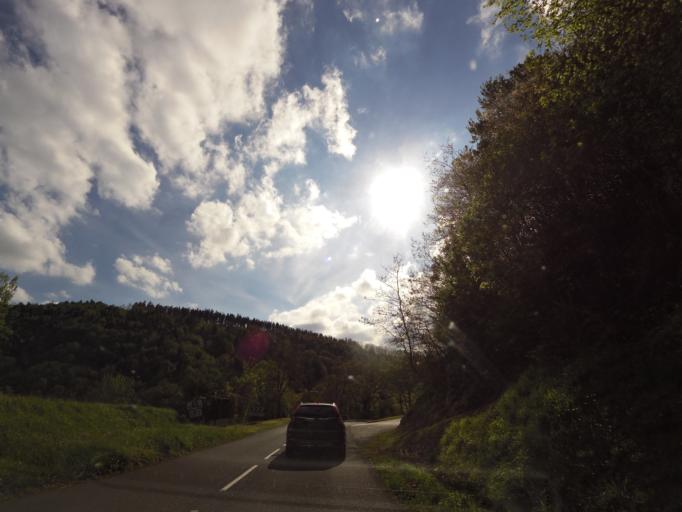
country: FR
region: Midi-Pyrenees
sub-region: Departement du Tarn
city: Soreze
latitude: 43.4314
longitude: 2.0544
